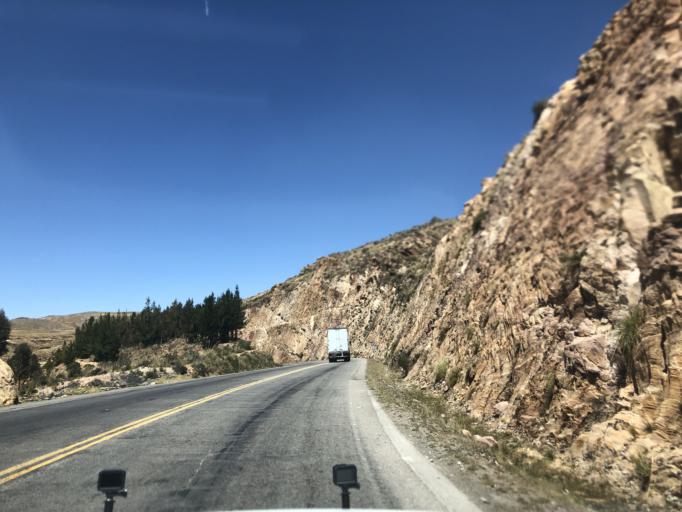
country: BO
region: Cochabamba
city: Irpa Irpa
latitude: -17.7012
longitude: -66.4805
